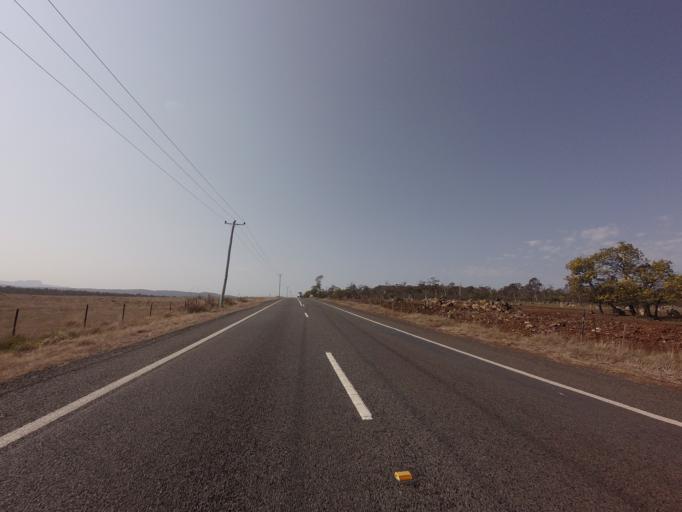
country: AU
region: Tasmania
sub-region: Northern Midlands
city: Evandale
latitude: -41.8338
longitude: 147.4644
